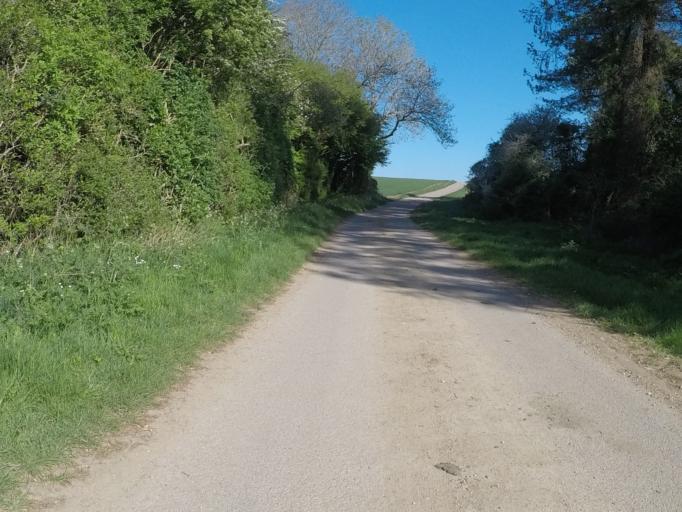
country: GB
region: England
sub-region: Oxfordshire
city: Stonesfield
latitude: 51.8567
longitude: -1.4443
